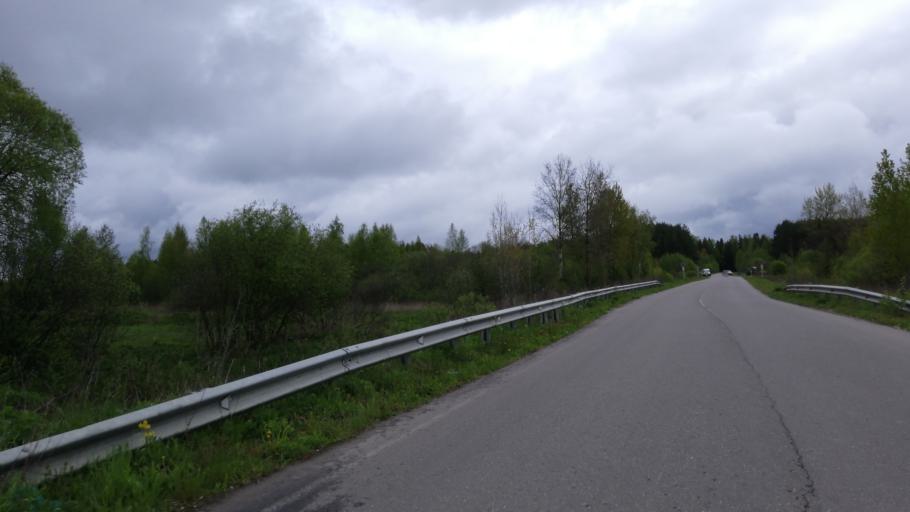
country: RU
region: Ivanovo
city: Novo-Talitsy
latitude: 57.0186
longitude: 40.7664
